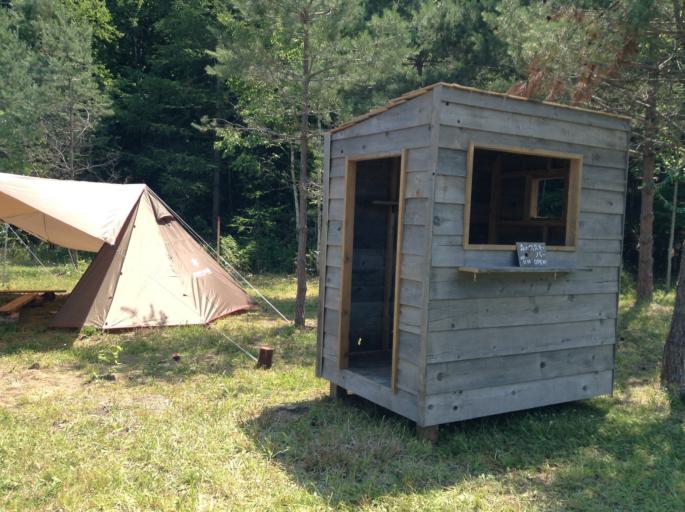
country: JP
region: Hokkaido
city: Nayoro
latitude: 44.2957
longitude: 142.6310
